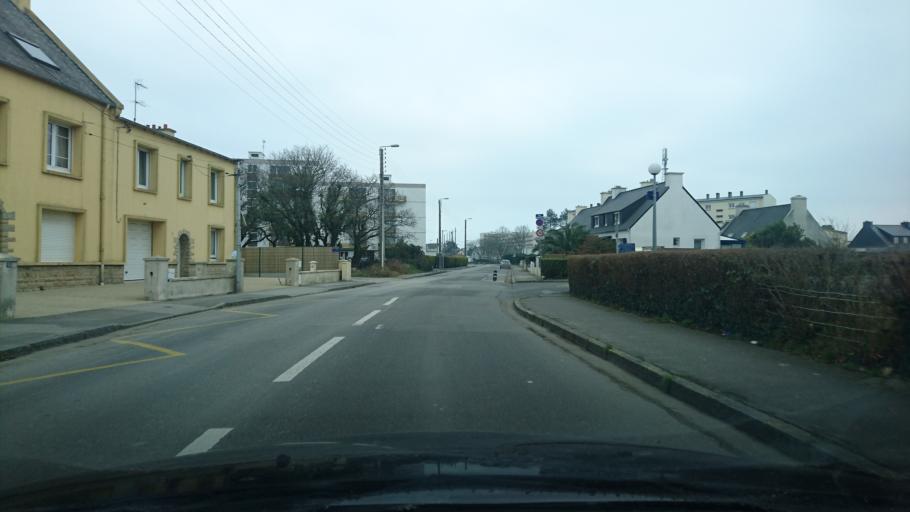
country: FR
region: Brittany
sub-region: Departement du Finistere
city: Brest
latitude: 48.3854
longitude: -4.5277
